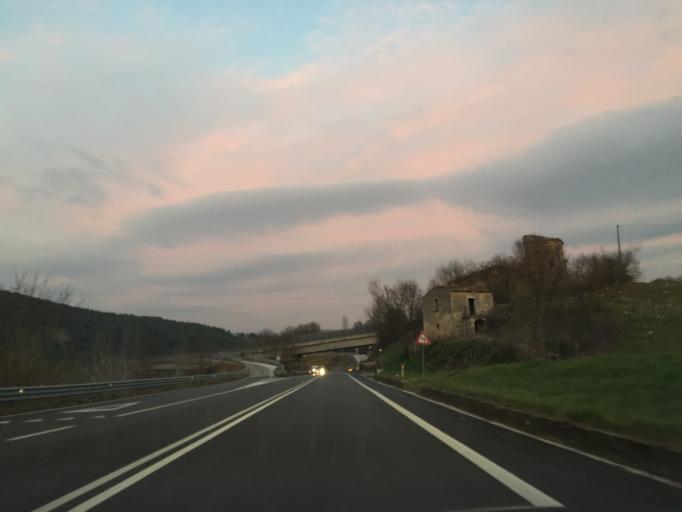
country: IT
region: Molise
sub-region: Provincia di Campobasso
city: Gambatesa
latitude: 41.5253
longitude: 14.9084
